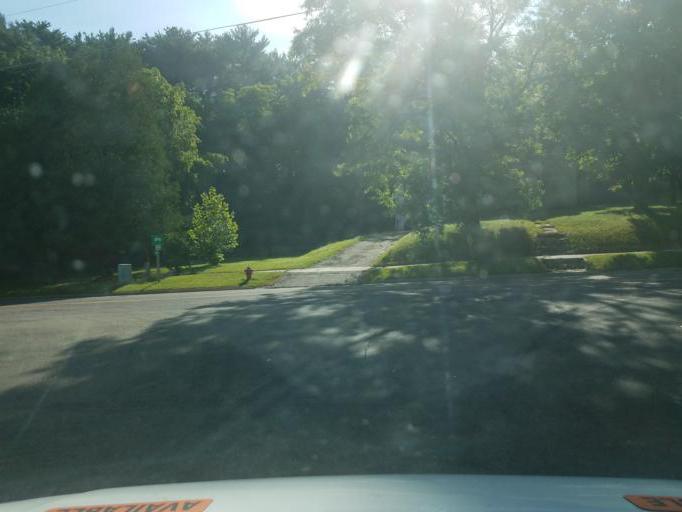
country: US
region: Wisconsin
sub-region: Sauk County
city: Reedsburg
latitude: 43.5798
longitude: -90.1345
